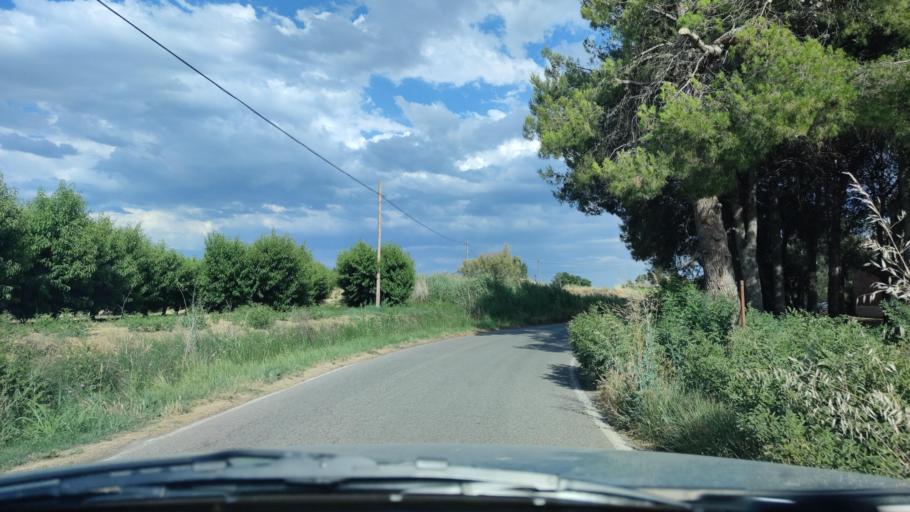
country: ES
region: Catalonia
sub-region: Provincia de Lleida
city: Alpicat
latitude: 41.6288
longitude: 0.5702
